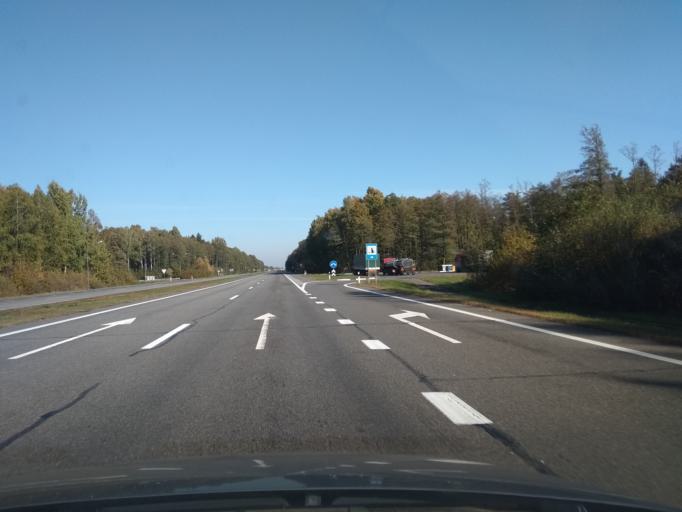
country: BY
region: Brest
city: Ivatsevichy
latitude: 52.6851
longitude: 25.3364
